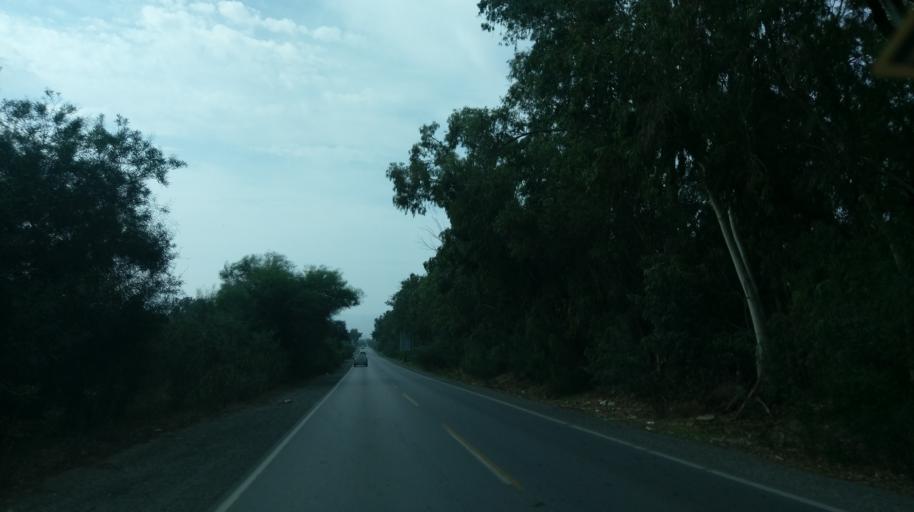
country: CY
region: Lefkosia
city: Lefka
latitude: 35.1538
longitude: 32.8659
